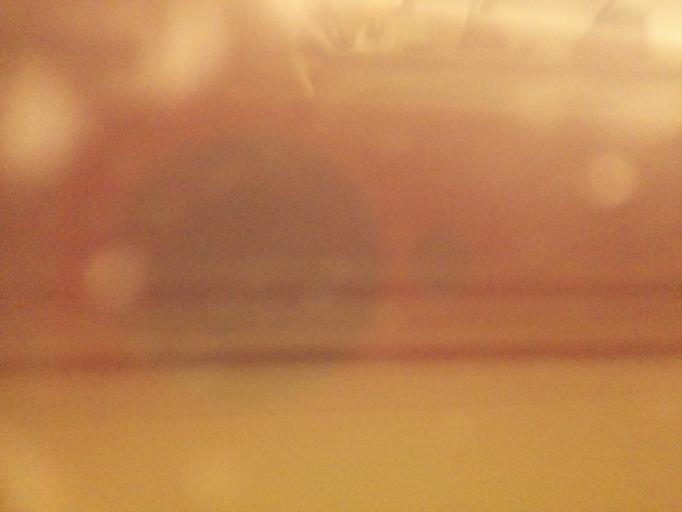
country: JP
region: Kanagawa
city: Ninomiya
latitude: 35.2959
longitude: 139.2162
